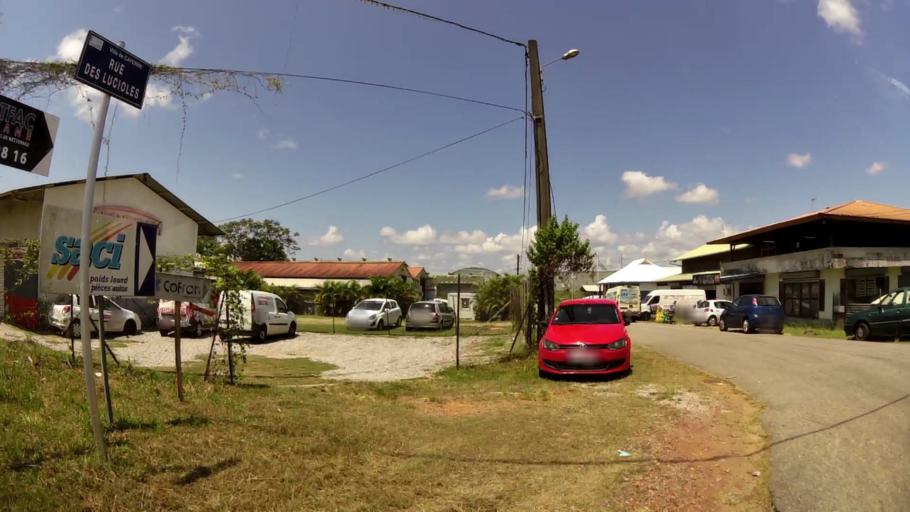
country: GF
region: Guyane
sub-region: Guyane
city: Cayenne
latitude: 4.9038
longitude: -52.3190
